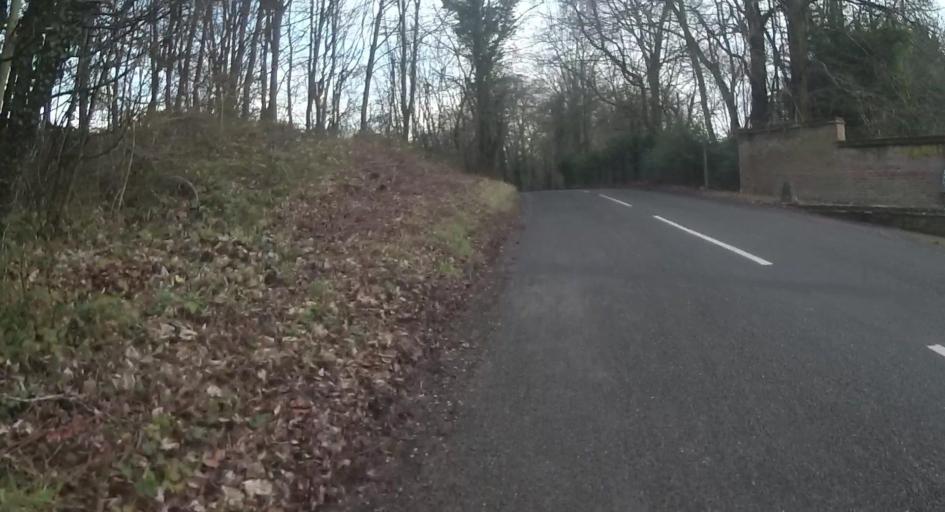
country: GB
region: England
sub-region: Hampshire
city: Highclere
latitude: 51.2278
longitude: -1.3806
